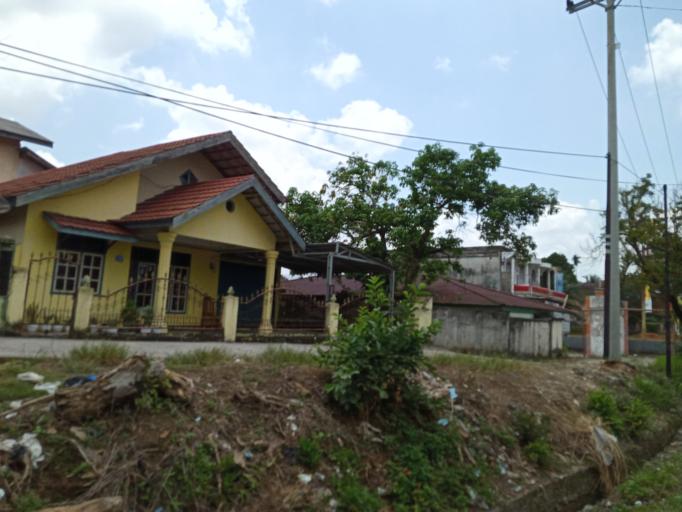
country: ID
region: Jambi
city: Bangko
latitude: -2.0857
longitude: 102.2613
